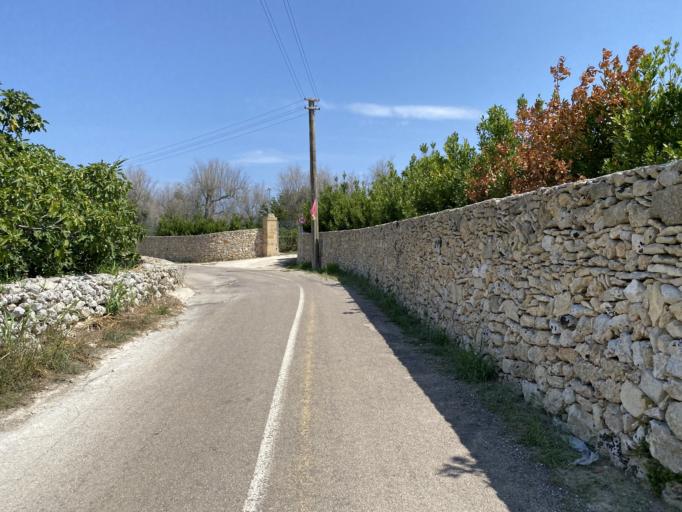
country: IT
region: Apulia
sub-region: Provincia di Lecce
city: Sanarica
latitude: 40.0944
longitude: 18.3533
